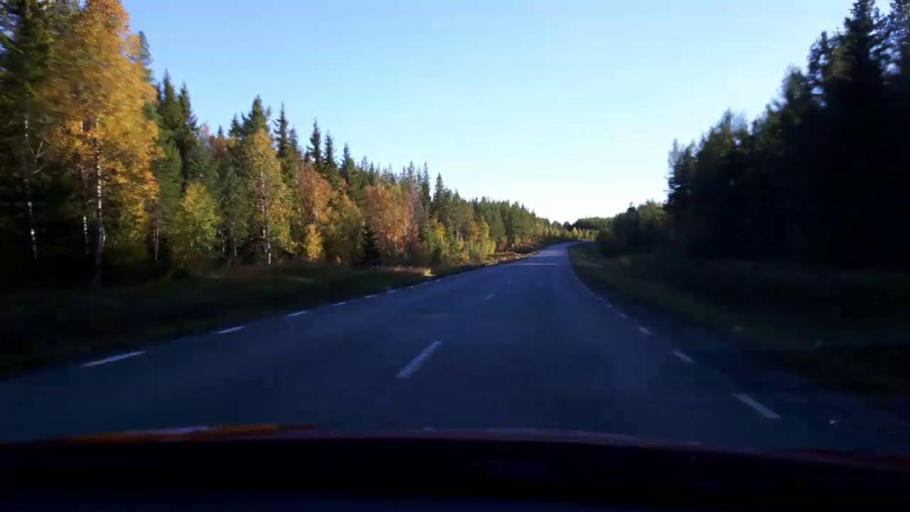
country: SE
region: Jaemtland
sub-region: OEstersunds Kommun
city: Lit
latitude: 63.7647
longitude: 14.7222
